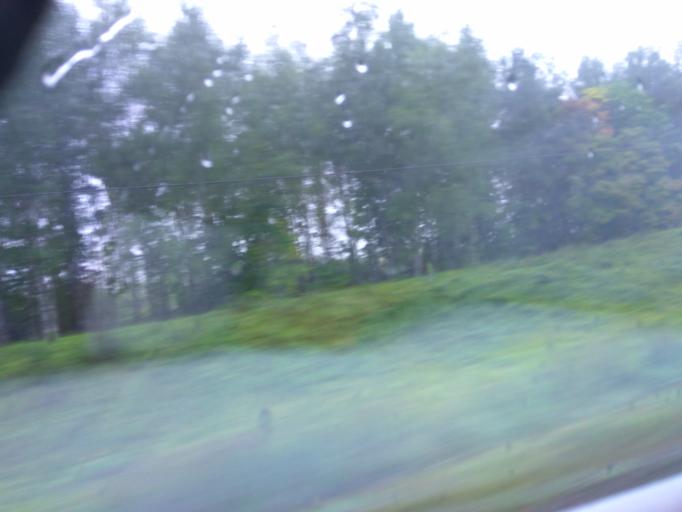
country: RU
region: Moskovskaya
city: Uzunovo
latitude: 54.6356
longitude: 38.5769
